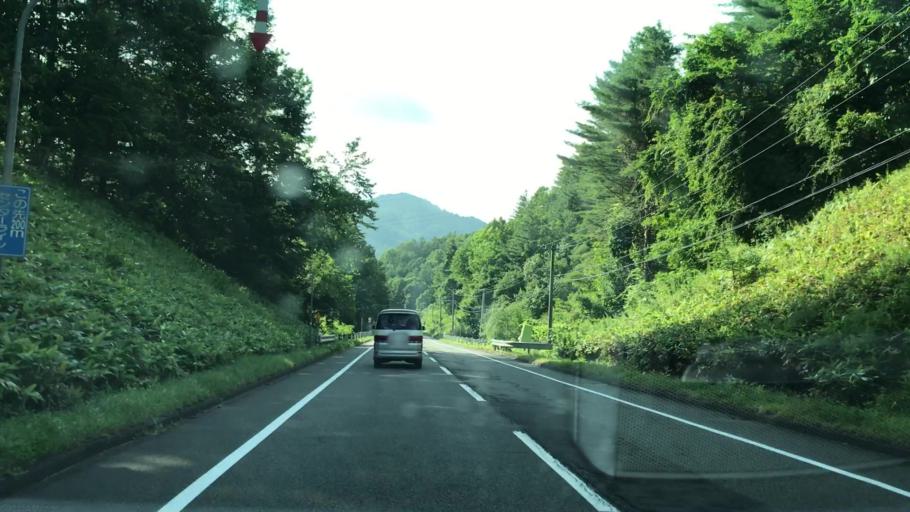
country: JP
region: Hokkaido
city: Shimo-furano
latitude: 42.8890
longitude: 142.1989
